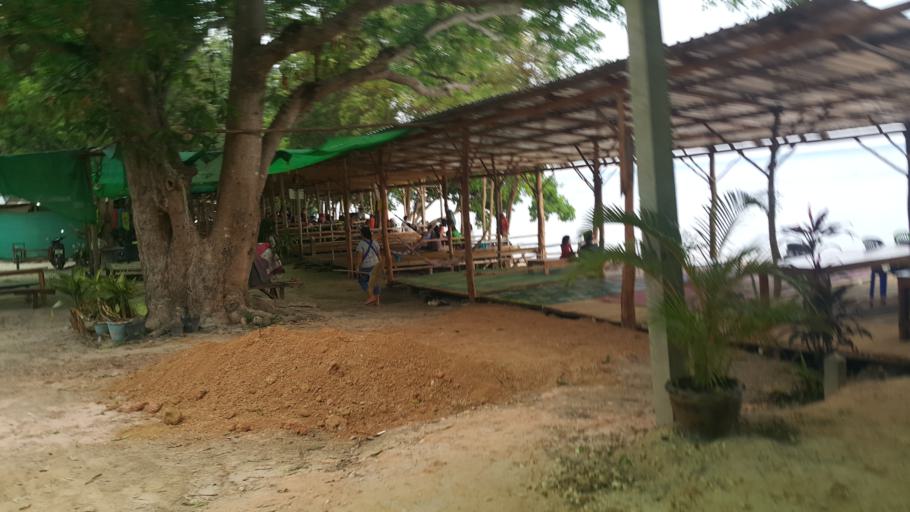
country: TH
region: Nong Khai
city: Bueng Khong Long
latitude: 17.9819
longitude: 104.0268
